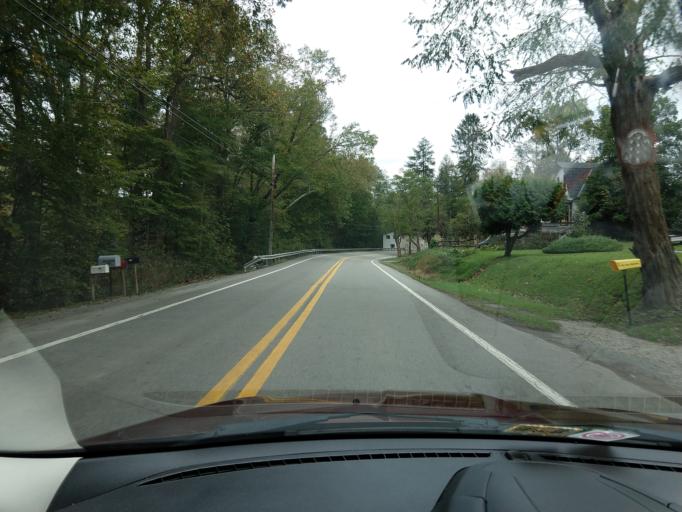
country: US
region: West Virginia
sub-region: Barbour County
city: Belington
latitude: 39.0038
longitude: -79.9389
